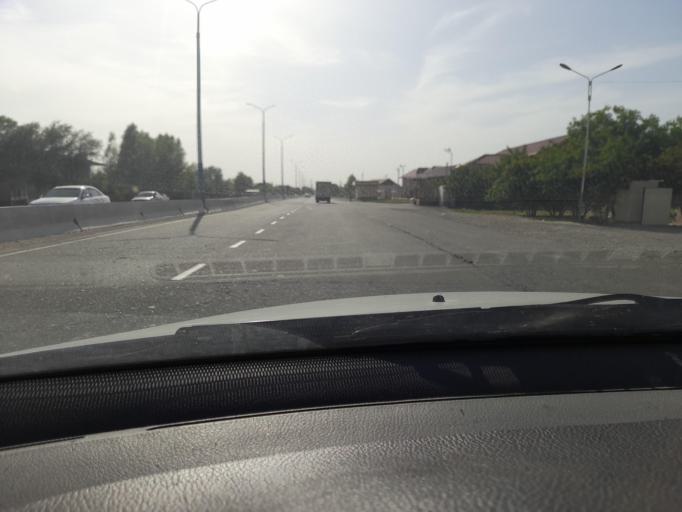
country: UZ
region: Samarqand
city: Kattaqo'rg'on
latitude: 39.9233
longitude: 66.2832
